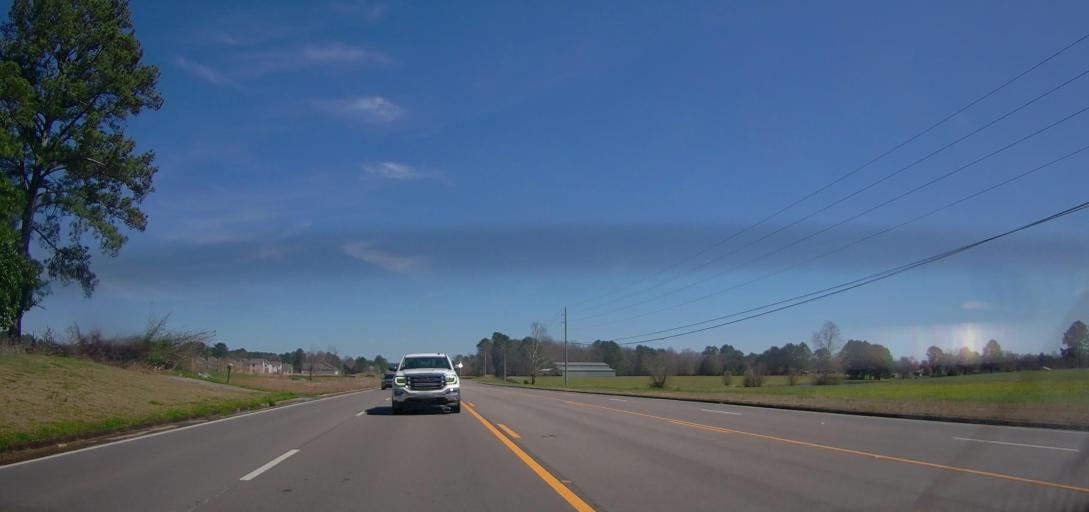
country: US
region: Alabama
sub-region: Cullman County
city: Cullman
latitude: 34.1784
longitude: -86.7409
